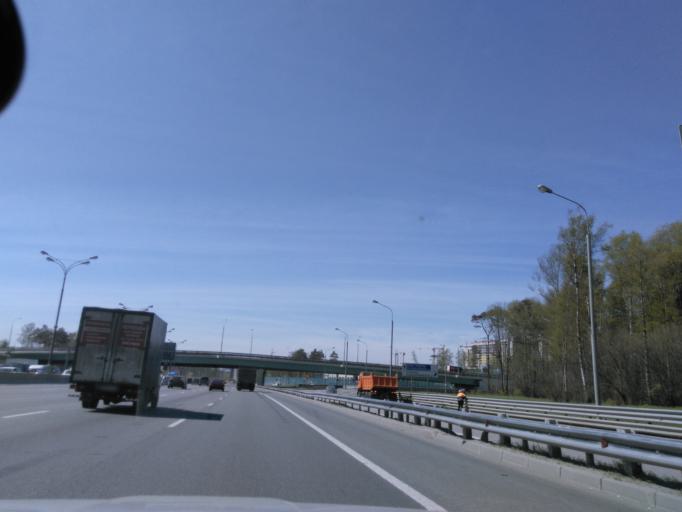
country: RU
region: Moscow
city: Khimki
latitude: 55.8723
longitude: 37.4144
